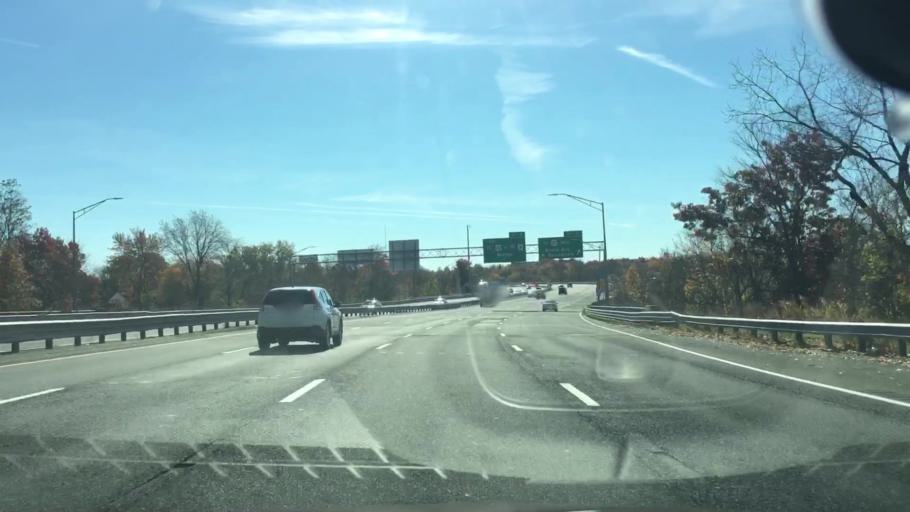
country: US
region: Massachusetts
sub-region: Hampden County
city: West Springfield
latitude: 42.1232
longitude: -72.6084
